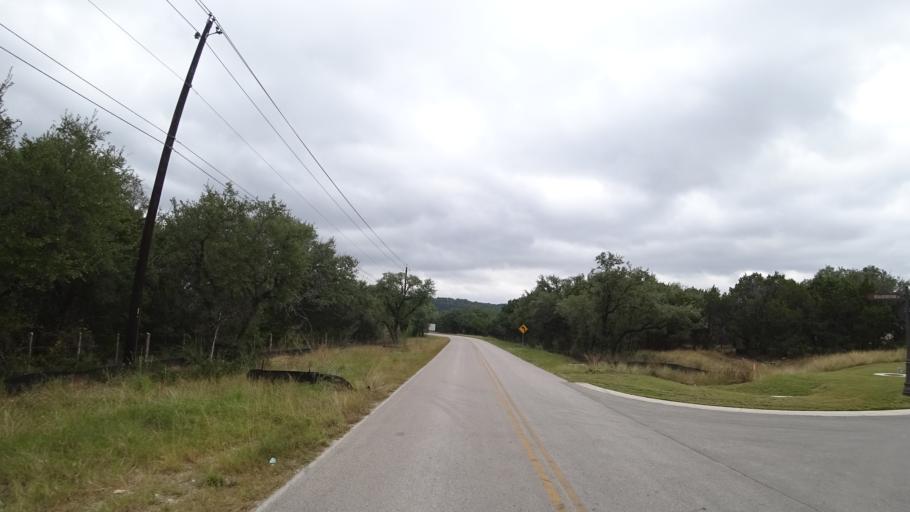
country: US
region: Texas
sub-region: Travis County
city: Bee Cave
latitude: 30.3372
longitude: -97.9146
